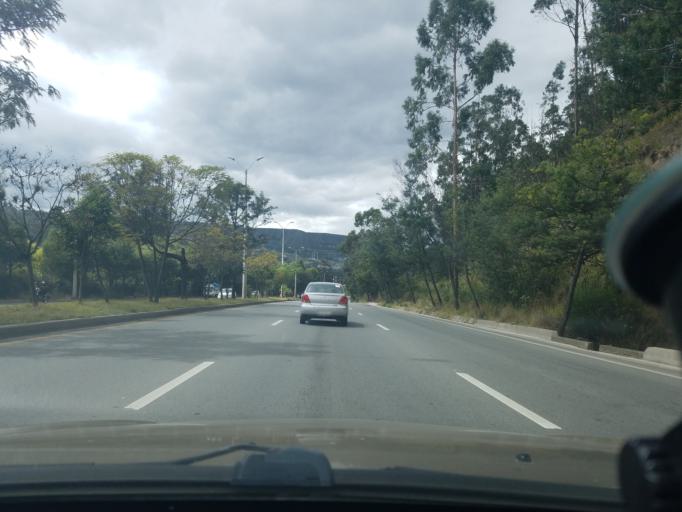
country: EC
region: Azuay
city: Llacao
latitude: -2.8699
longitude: -78.9368
